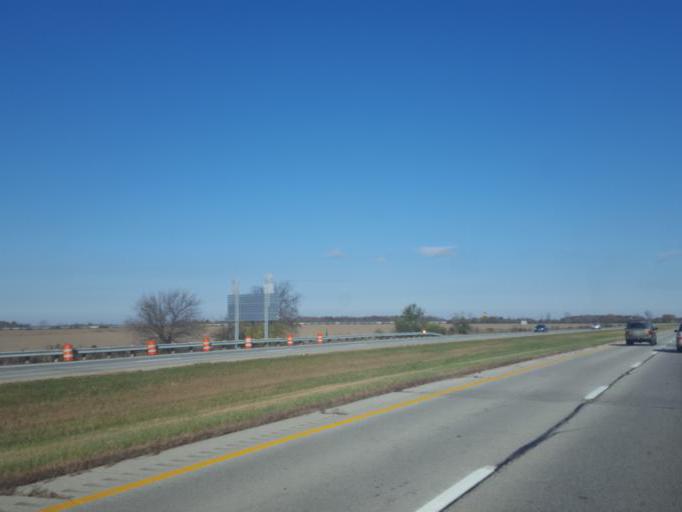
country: US
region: Ohio
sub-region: Marion County
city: Marion
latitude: 40.6320
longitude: -83.0972
